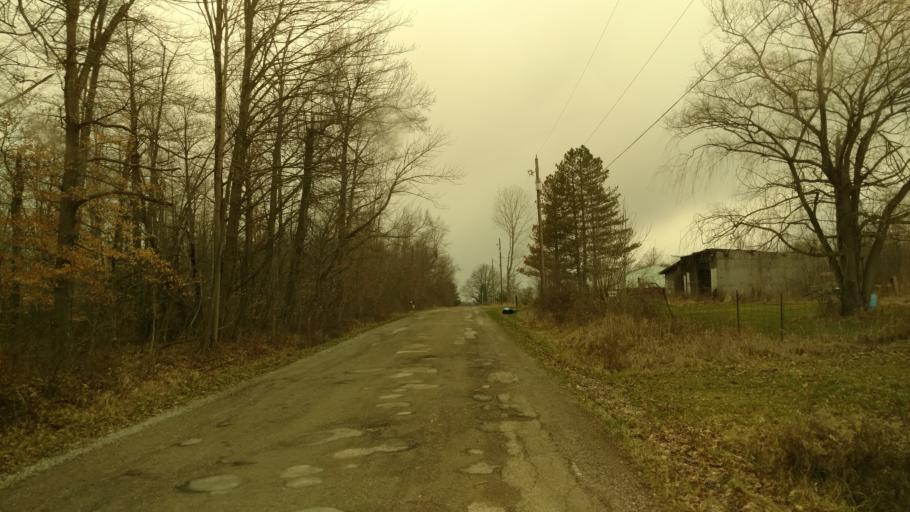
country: US
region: Ohio
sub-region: Crawford County
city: Galion
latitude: 40.6786
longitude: -82.7795
